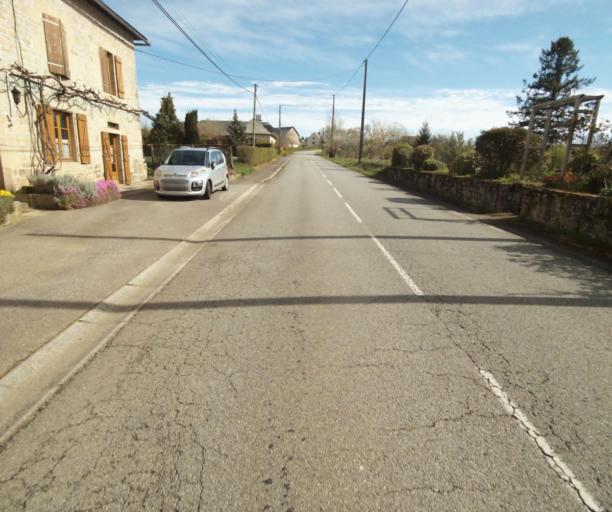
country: FR
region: Limousin
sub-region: Departement de la Correze
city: Laguenne
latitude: 45.2749
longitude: 1.8235
